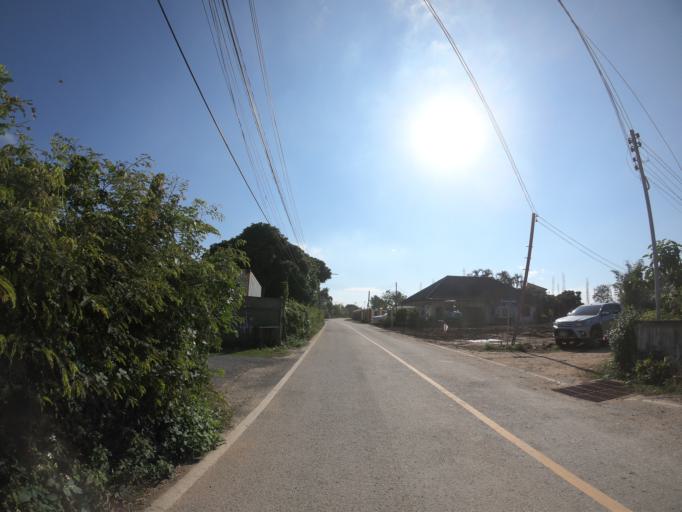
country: TH
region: Chiang Mai
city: Saraphi
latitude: 18.7094
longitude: 99.0005
